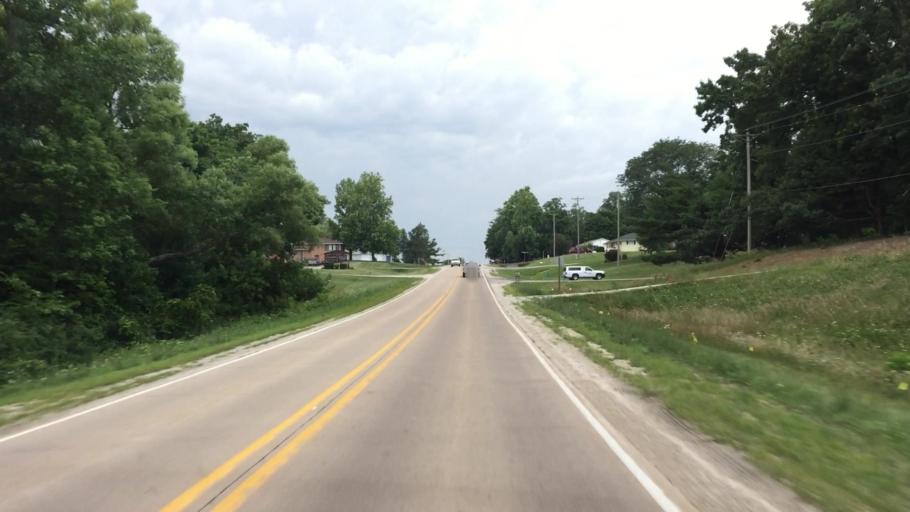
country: US
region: Iowa
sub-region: Lee County
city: Fort Madison
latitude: 40.6462
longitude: -91.3175
